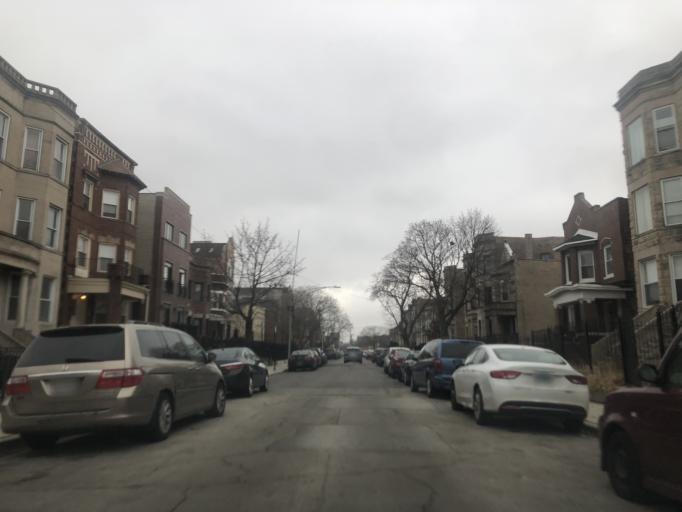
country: US
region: Illinois
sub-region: Cook County
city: Chicago
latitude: 41.7791
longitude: -87.6016
